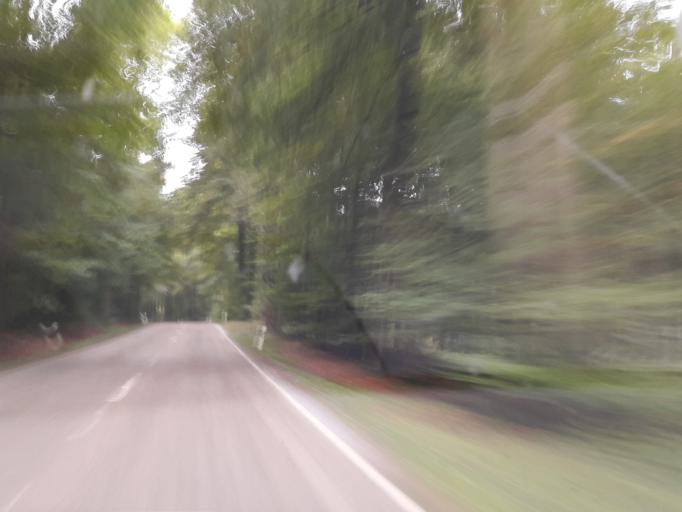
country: DE
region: Baden-Wuerttemberg
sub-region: Regierungsbezirk Stuttgart
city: Mockmuhl
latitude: 49.2792
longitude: 9.3485
